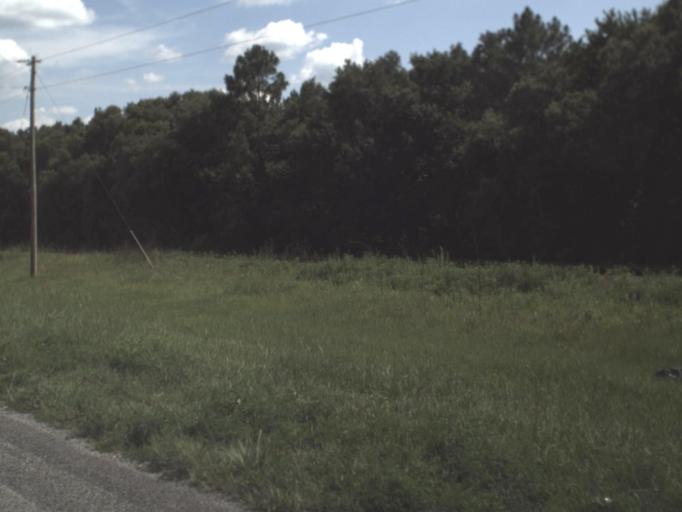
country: US
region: Florida
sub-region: Alachua County
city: Waldo
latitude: 29.6935
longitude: -82.1299
